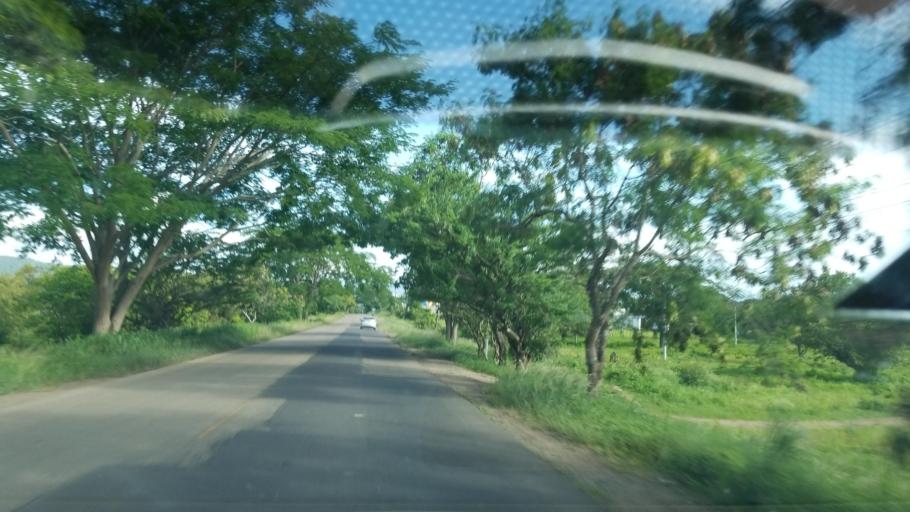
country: HN
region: El Paraiso
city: Arauli
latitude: 13.9511
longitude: -86.5607
